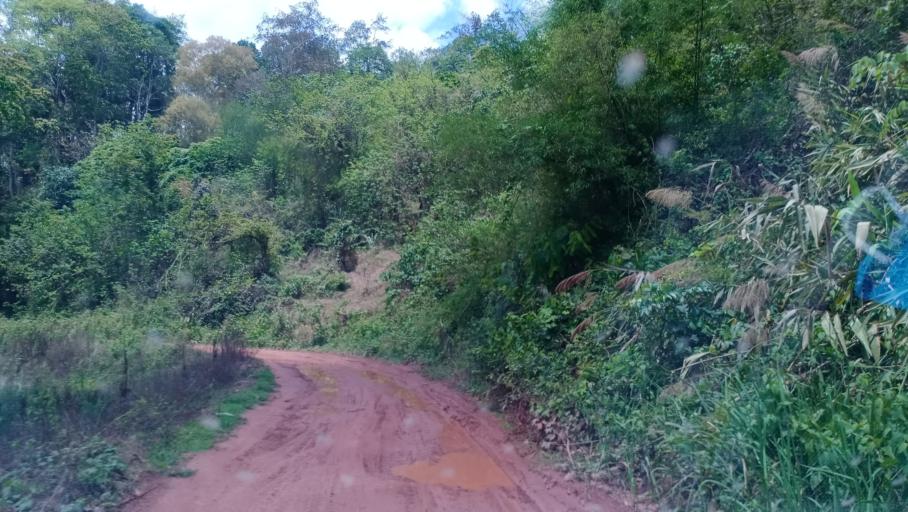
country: CN
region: Yunnan
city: Menglie
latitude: 22.1417
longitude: 101.7791
